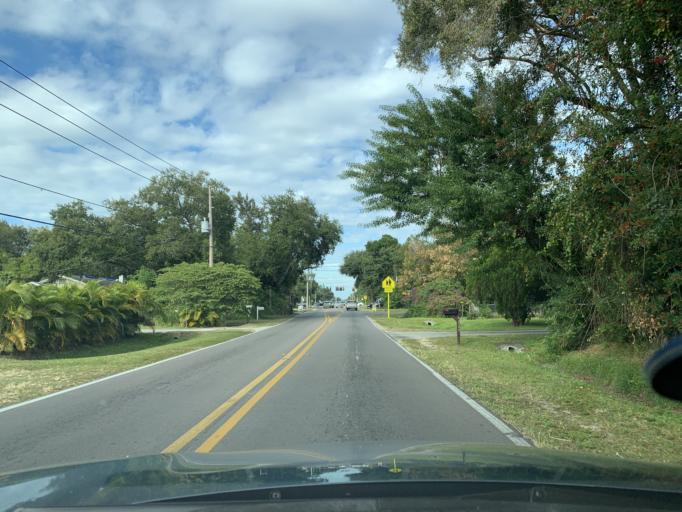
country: US
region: Florida
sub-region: Pinellas County
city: Kenneth City
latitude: 27.8194
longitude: -82.7367
